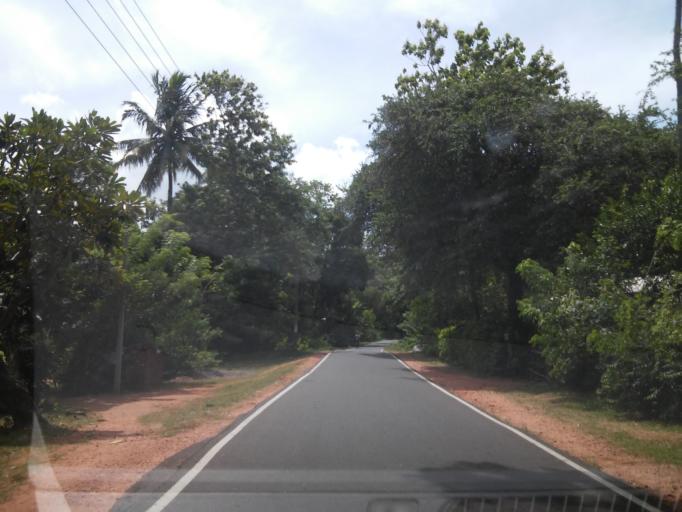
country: LK
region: North Central
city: Anuradhapura
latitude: 8.3632
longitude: 80.4003
